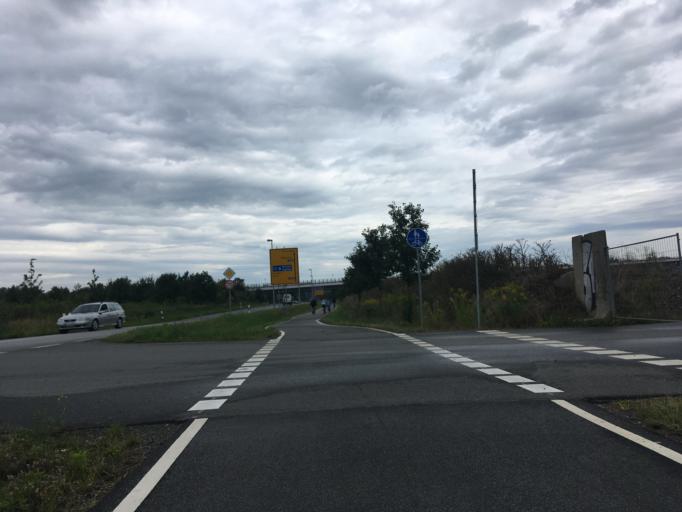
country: DE
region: Saxony
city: Pirna
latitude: 50.9661
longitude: 13.9119
